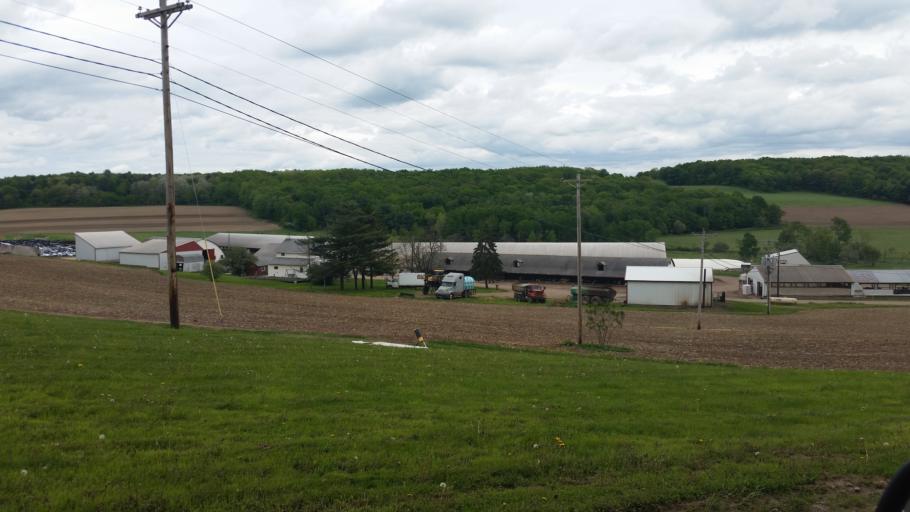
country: US
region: Pennsylvania
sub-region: Tioga County
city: Westfield
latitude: 41.9542
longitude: -77.7253
